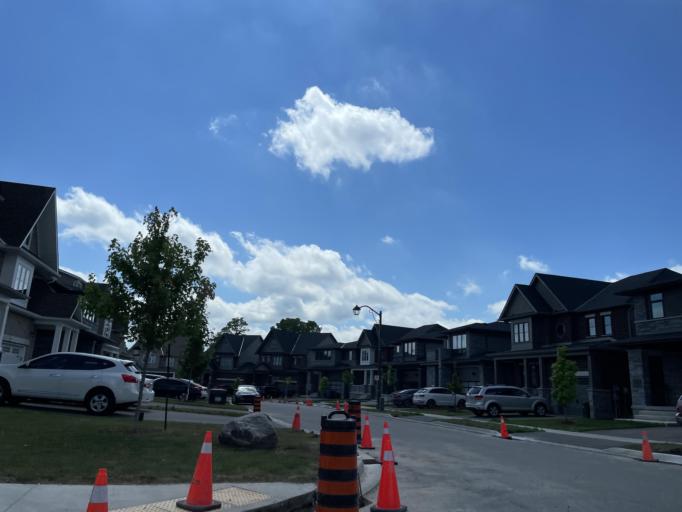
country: CA
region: Ontario
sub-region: Wellington County
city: Guelph
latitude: 43.5154
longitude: -80.2134
